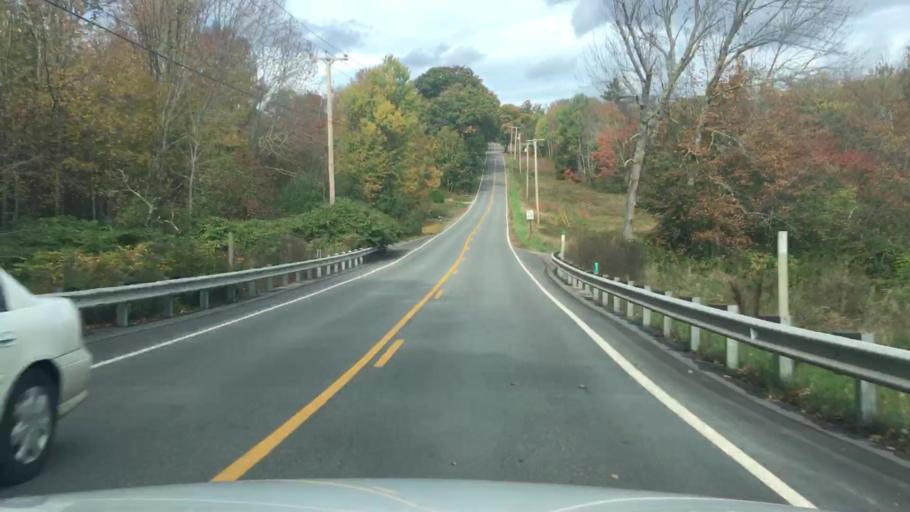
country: US
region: Maine
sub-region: Knox County
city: Hope
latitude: 44.2996
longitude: -69.1093
